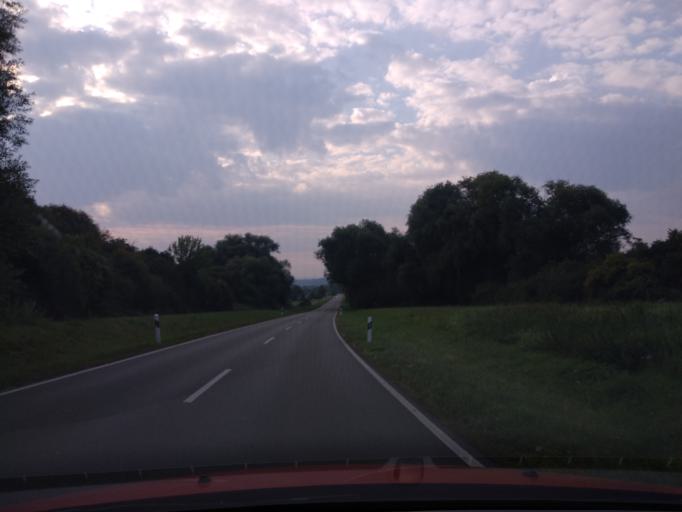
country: DE
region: Hesse
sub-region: Regierungsbezirk Kassel
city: Calden
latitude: 51.3767
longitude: 9.3794
